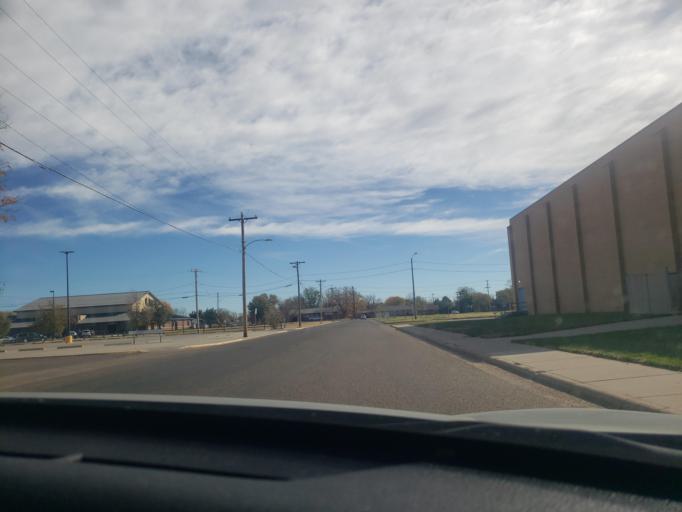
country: US
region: Kansas
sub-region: Finney County
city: Garden City
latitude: 37.9790
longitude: -100.8679
